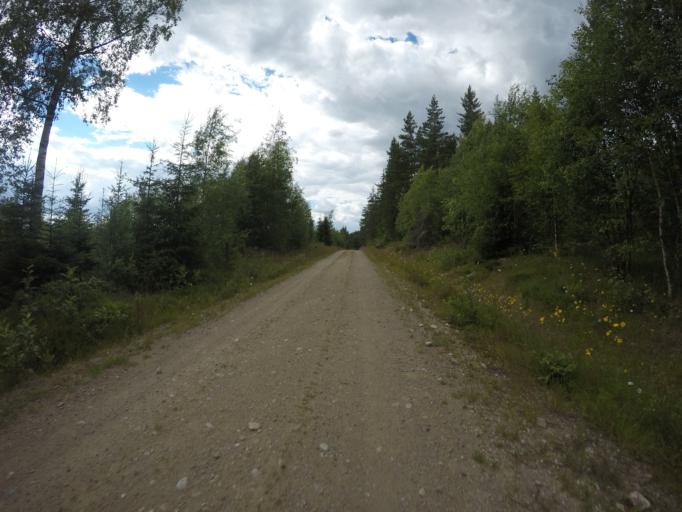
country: SE
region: Vaermland
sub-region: Filipstads Kommun
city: Lesjofors
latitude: 60.0699
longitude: 14.4584
